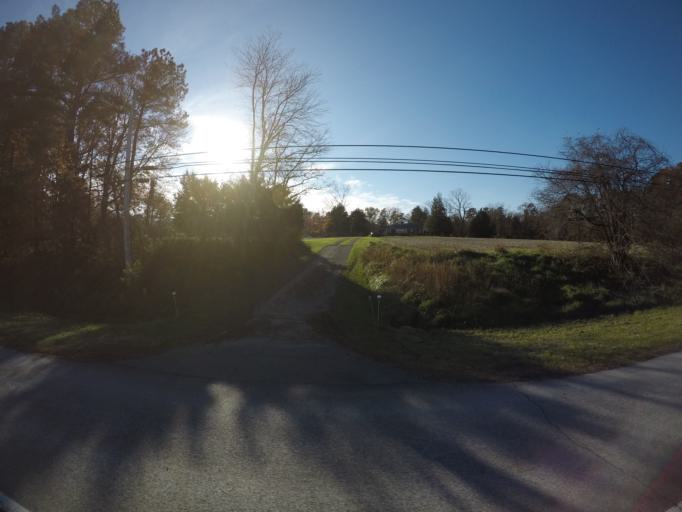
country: US
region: Maryland
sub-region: Saint Mary's County
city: Leonardtown
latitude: 38.3473
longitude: -76.6766
